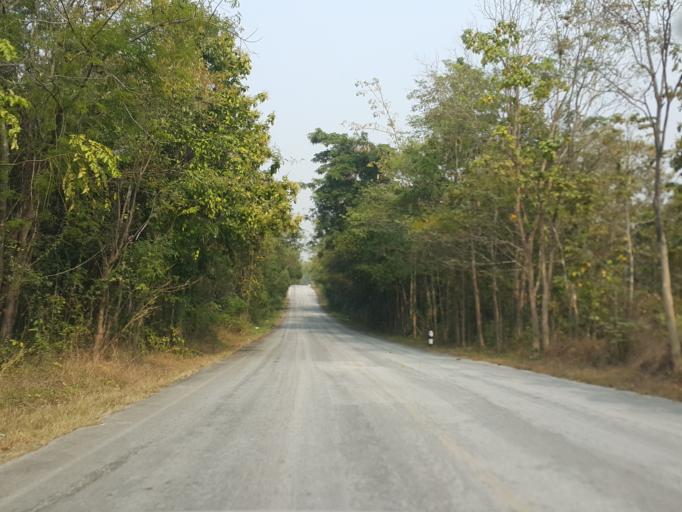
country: TH
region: Lampang
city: Thoen
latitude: 17.6327
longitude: 99.2732
